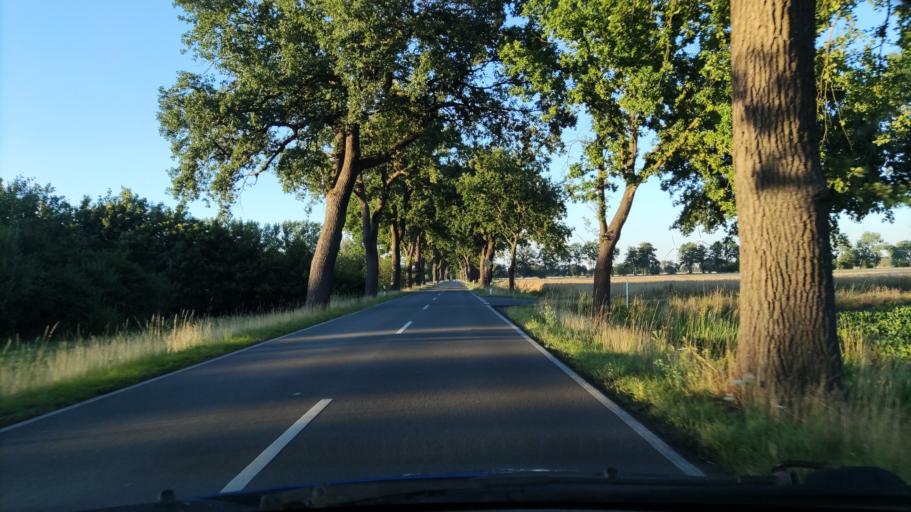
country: DE
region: Lower Saxony
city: Luechow
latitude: 52.9829
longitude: 11.1672
